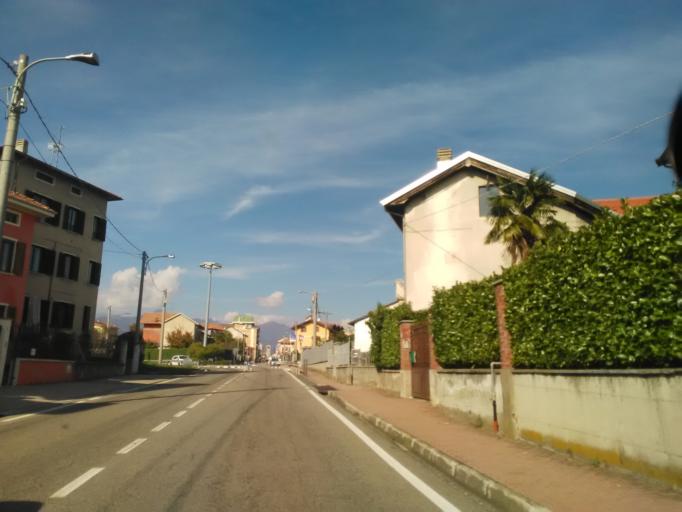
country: IT
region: Piedmont
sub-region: Provincia di Vercelli
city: Serravalle Sesia
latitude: 45.6804
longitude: 8.3168
